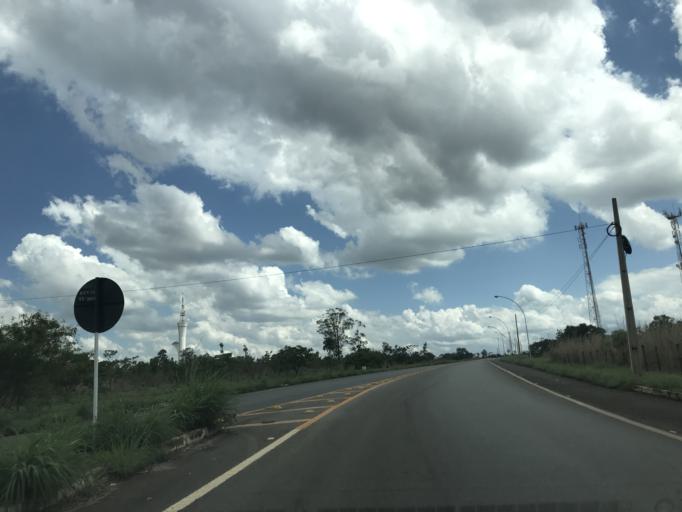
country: BR
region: Federal District
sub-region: Brasilia
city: Brasilia
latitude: -15.6898
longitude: -47.8344
